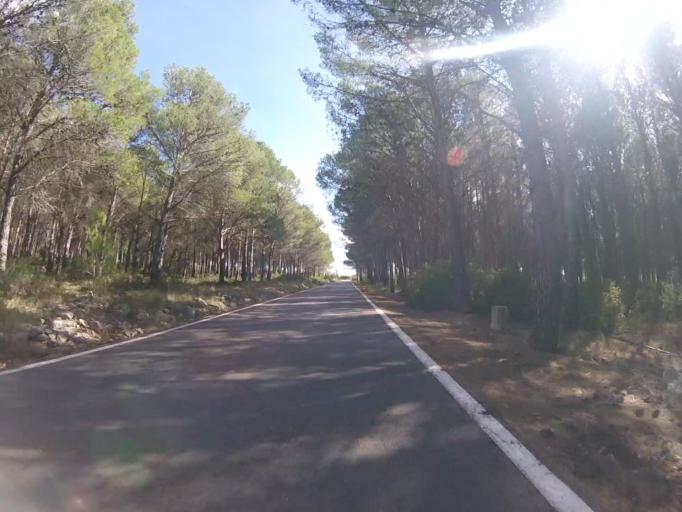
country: ES
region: Valencia
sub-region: Provincia de Castello
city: Albocasser
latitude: 40.4038
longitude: 0.0805
